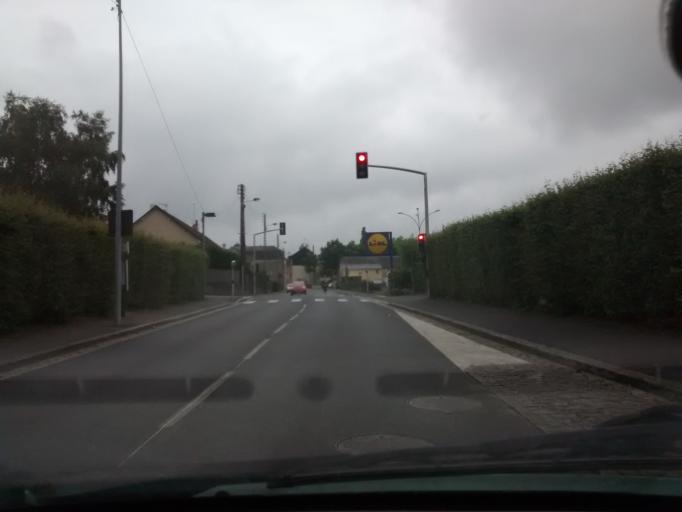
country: FR
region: Lower Normandy
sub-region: Departement de la Manche
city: Saint-Lo
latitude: 49.1107
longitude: -1.0957
